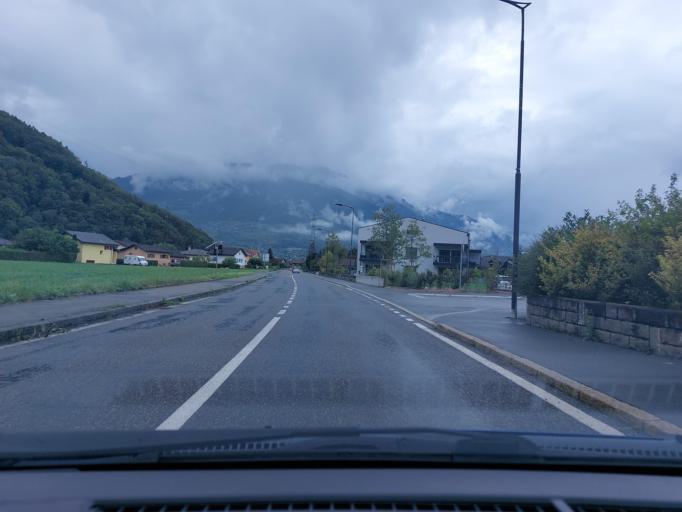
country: CH
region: Vaud
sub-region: Aigle District
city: Bex
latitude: 46.2429
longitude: 6.9875
